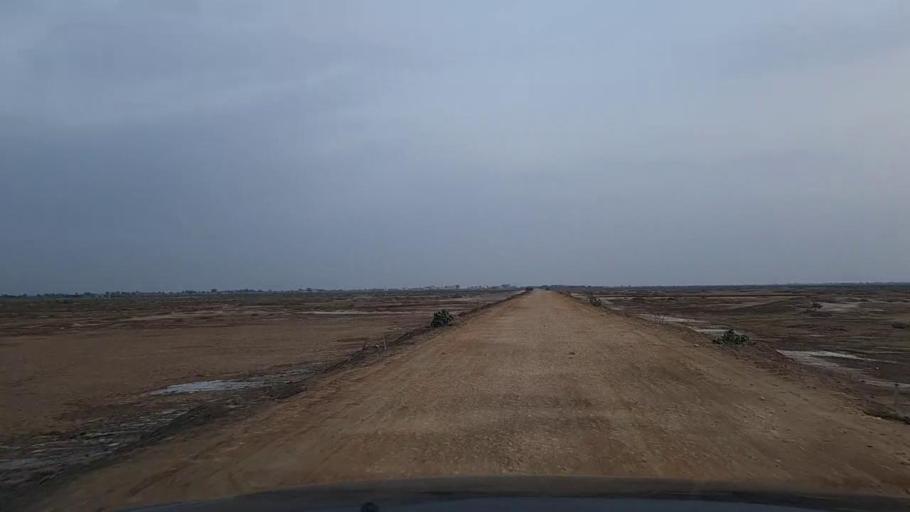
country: PK
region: Sindh
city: Jati
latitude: 24.4987
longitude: 68.3832
